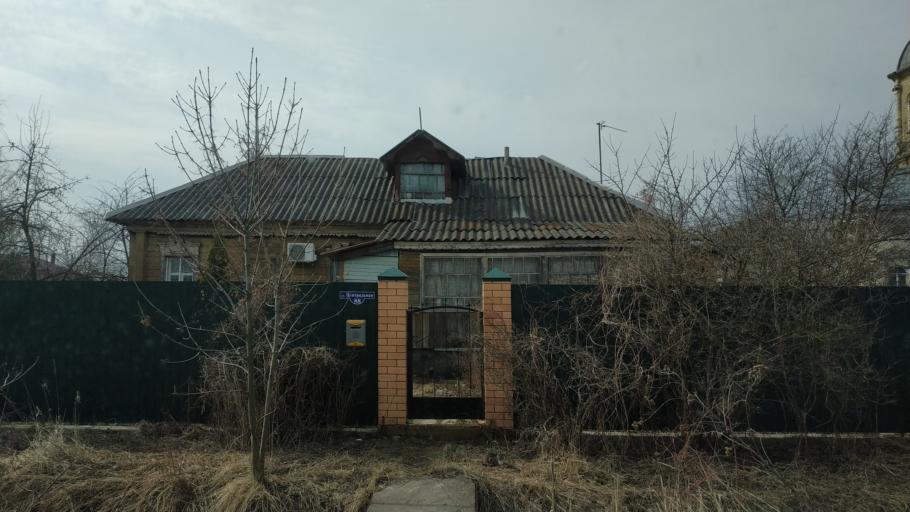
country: RU
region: Moskovskaya
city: Ashitkovo
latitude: 55.4220
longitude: 38.5482
